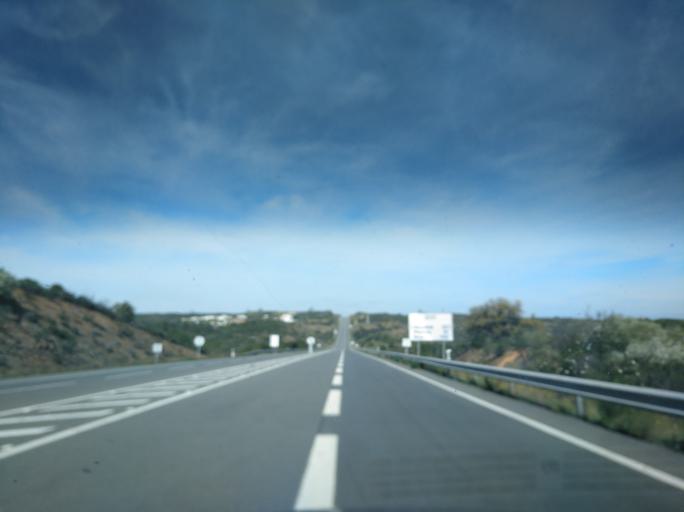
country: PT
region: Faro
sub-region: Castro Marim
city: Castro Marim
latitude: 37.2952
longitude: -7.4877
